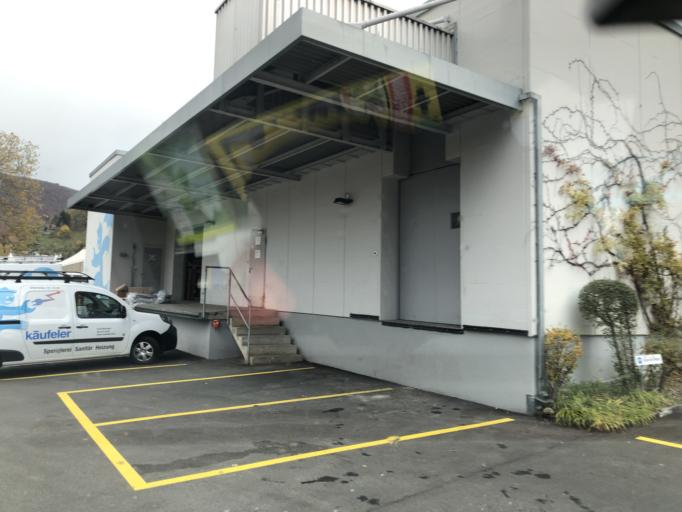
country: CH
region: Aargau
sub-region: Bezirk Baden
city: Neuenhof
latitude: 47.4588
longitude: 8.3339
